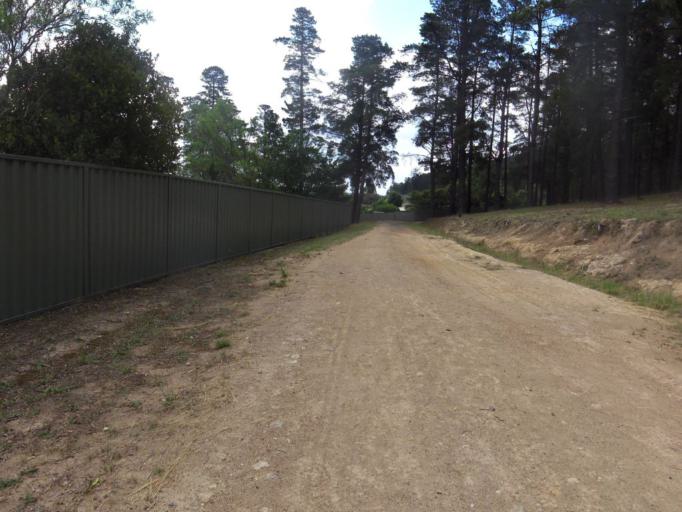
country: AU
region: Australian Capital Territory
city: Macarthur
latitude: -35.3708
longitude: 149.1163
